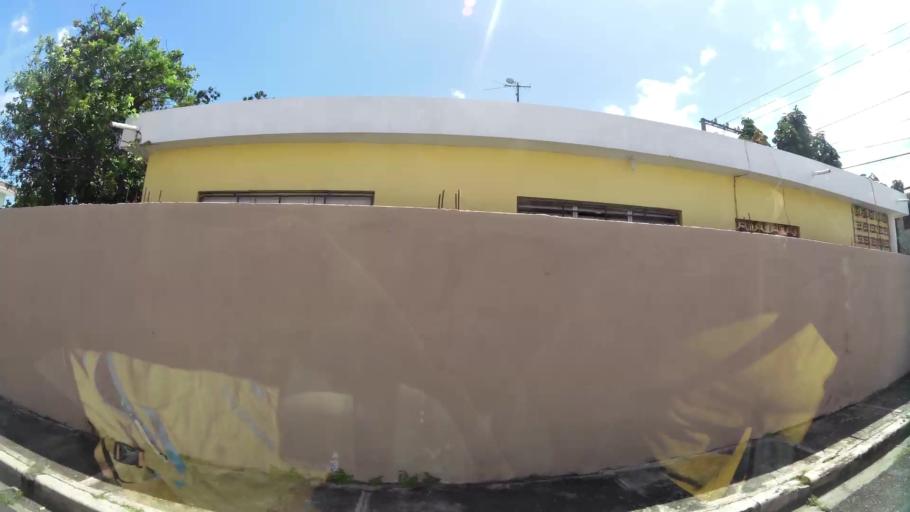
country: DO
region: San Cristobal
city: San Cristobal
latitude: 18.4183
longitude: -70.0957
